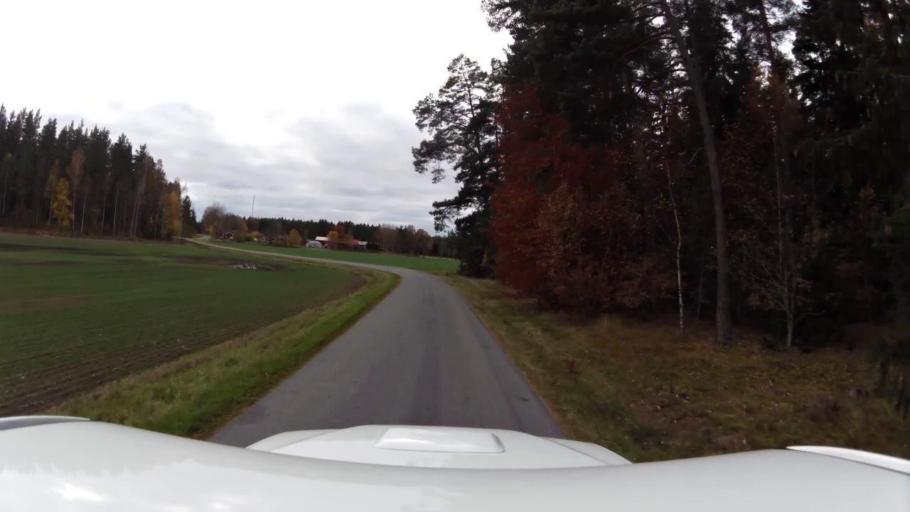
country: SE
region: OEstergoetland
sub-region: Linkopings Kommun
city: Linghem
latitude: 58.3977
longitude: 15.8394
